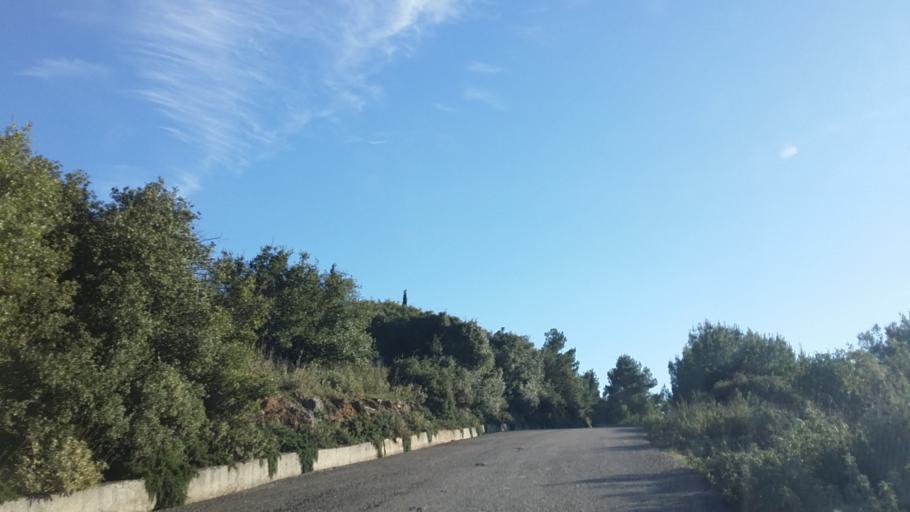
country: GR
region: West Greece
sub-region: Nomos Aitolias kai Akarnanias
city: Fitiai
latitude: 38.7012
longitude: 21.1841
